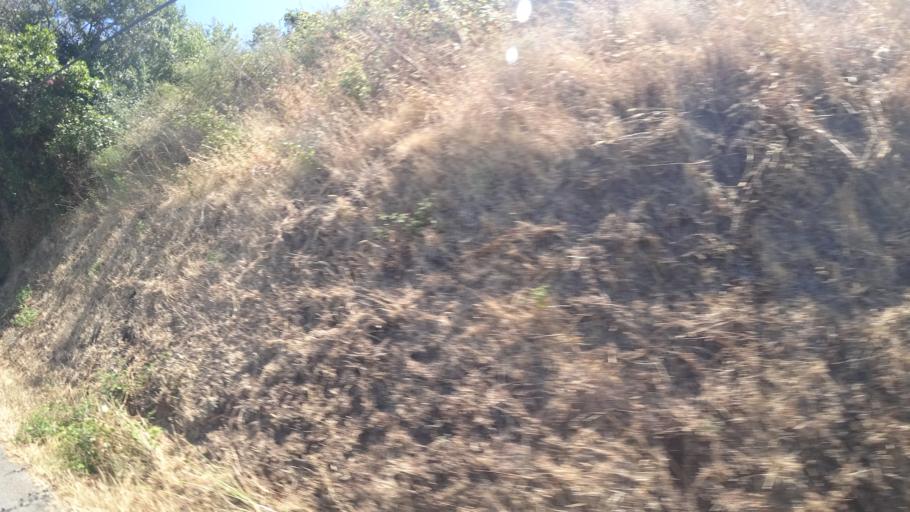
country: FR
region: Corsica
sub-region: Departement de la Corse-du-Sud
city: Alata
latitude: 41.9805
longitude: 8.6789
